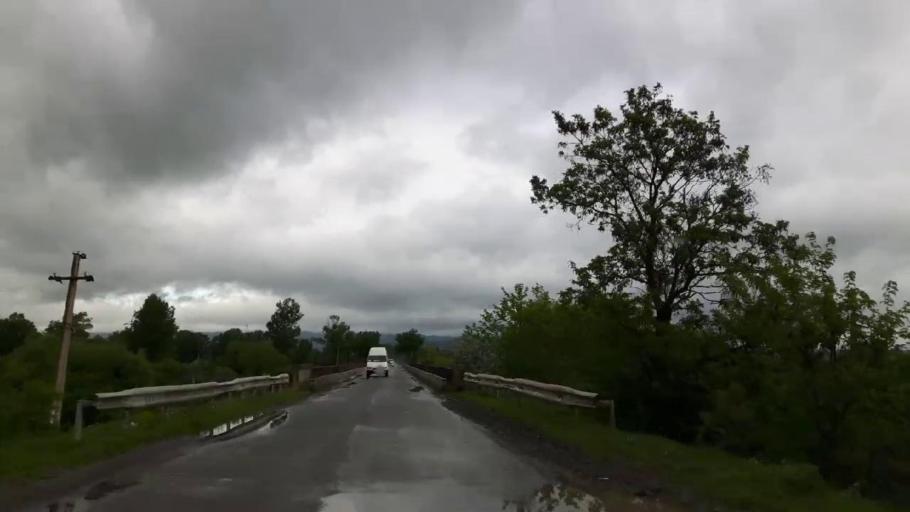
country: GE
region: Shida Kartli
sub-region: Khashuris Raioni
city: Khashuri
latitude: 41.9911
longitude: 43.6591
